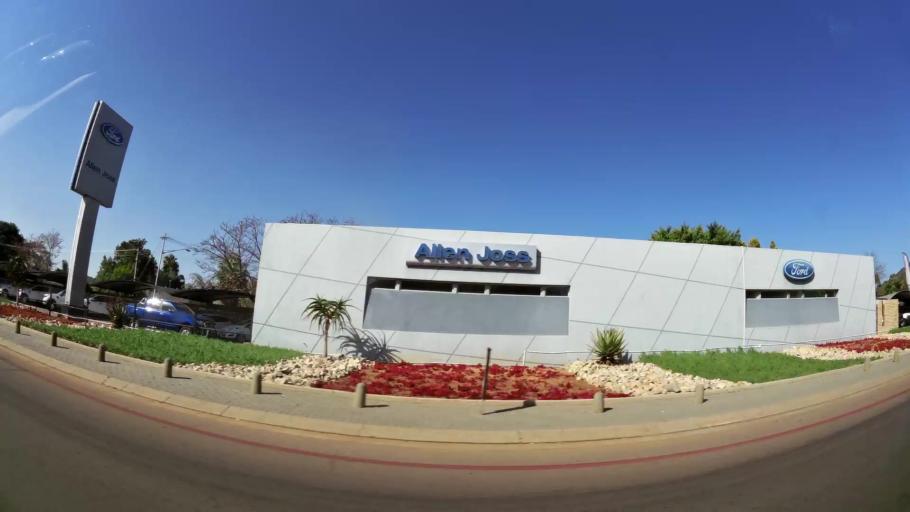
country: ZA
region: Gauteng
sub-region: City of Tshwane Metropolitan Municipality
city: Pretoria
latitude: -25.6812
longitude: 28.1940
